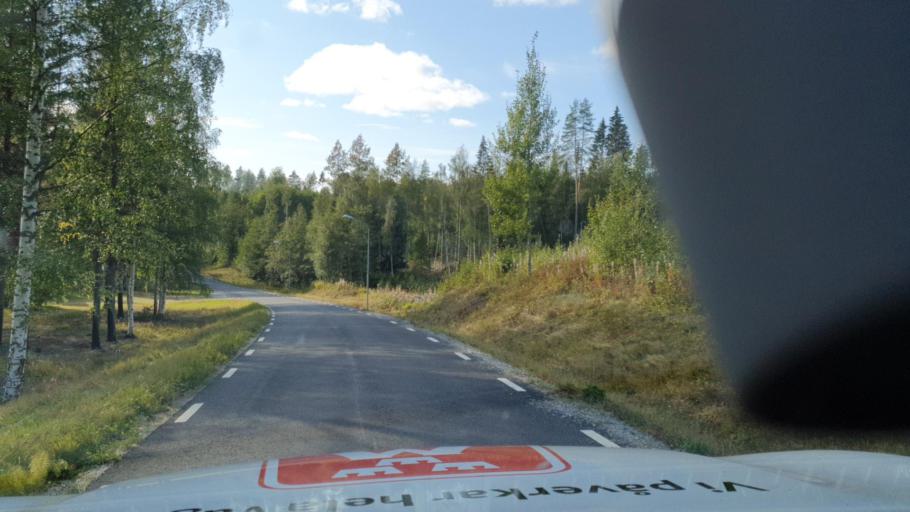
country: SE
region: Vaesterbotten
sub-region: Dorotea Kommun
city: Dorotea
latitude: 63.8590
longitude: 16.3629
